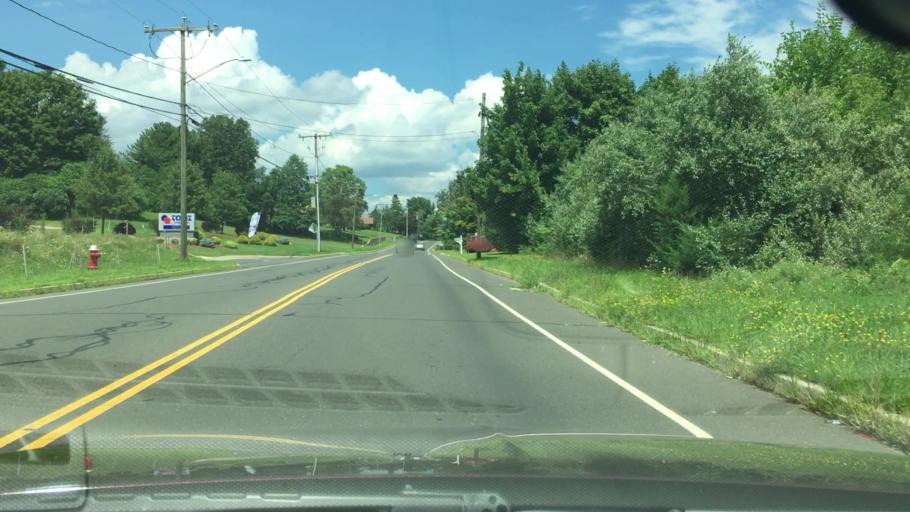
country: US
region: Connecticut
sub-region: Hartford County
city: Kensington
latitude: 41.6417
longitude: -72.7360
